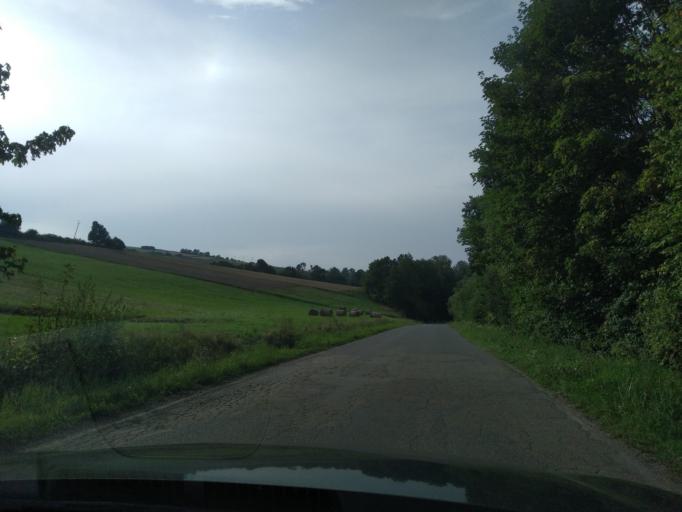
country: PL
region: Subcarpathian Voivodeship
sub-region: Powiat sanocki
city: Tyrawa Woloska
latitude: 49.5809
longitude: 22.3493
